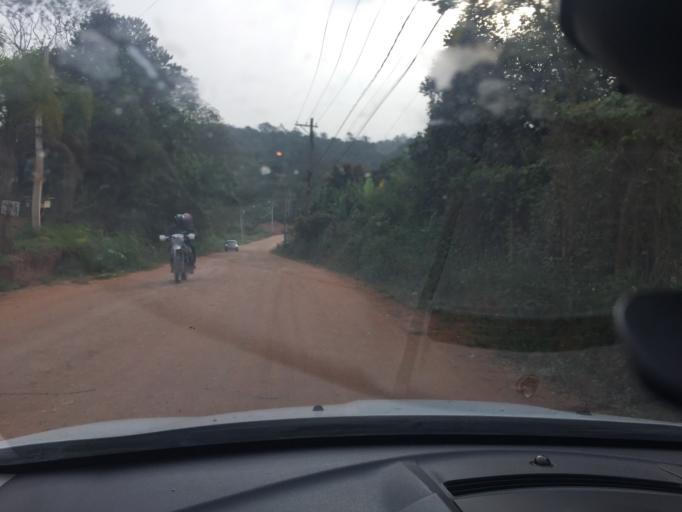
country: BR
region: Sao Paulo
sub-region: Campo Limpo Paulista
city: Campo Limpo Paulista
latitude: -23.1897
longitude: -46.7881
